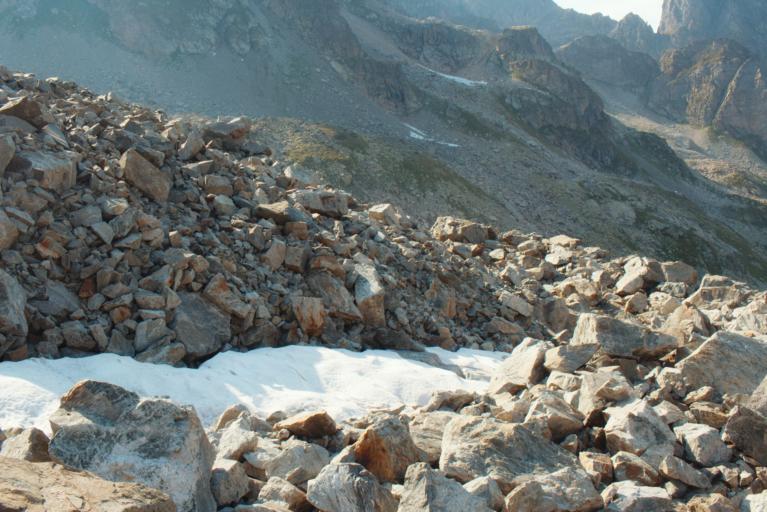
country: RU
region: Karachayevo-Cherkesiya
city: Nizhniy Arkhyz
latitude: 43.4580
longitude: 41.2253
